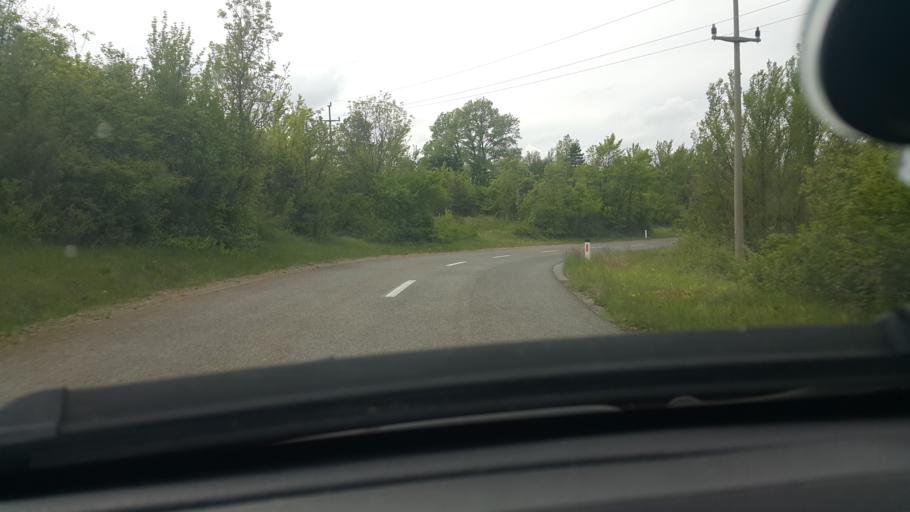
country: IT
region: Friuli Venezia Giulia
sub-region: Provincia di Trieste
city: Zolla
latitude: 45.7719
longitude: 13.7995
